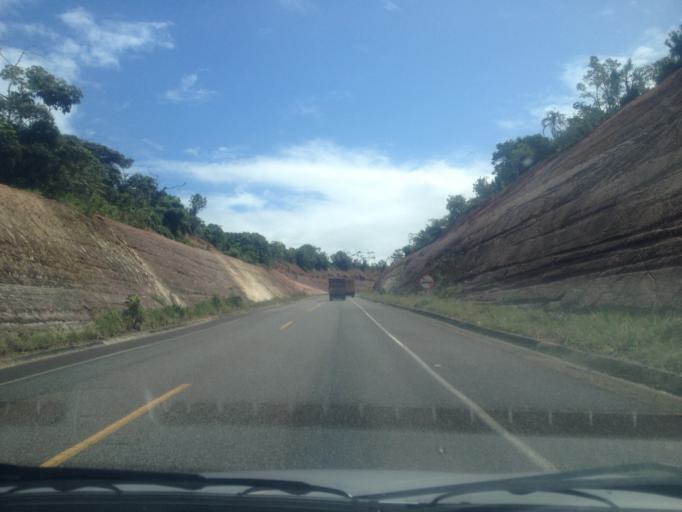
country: BR
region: Sergipe
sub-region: Indiaroba
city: Indiaroba
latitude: -11.5626
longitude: -37.5710
